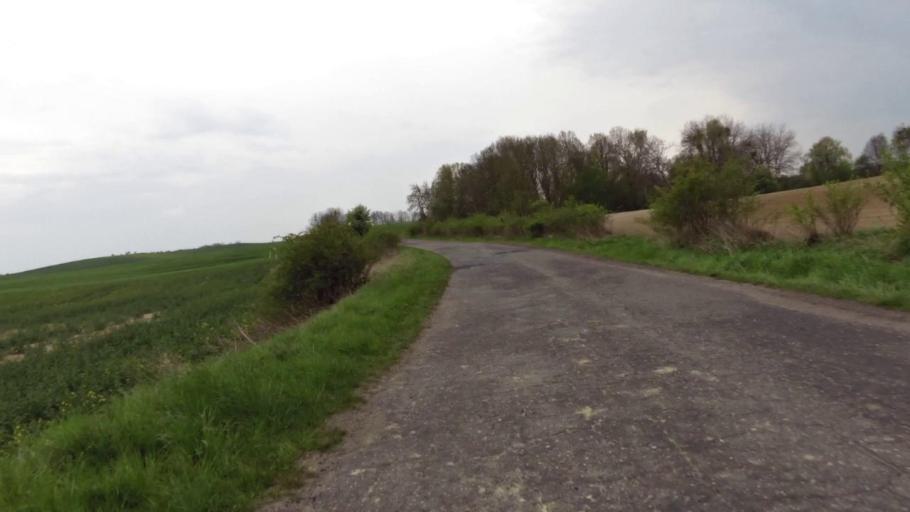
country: PL
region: West Pomeranian Voivodeship
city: Trzcinsko Zdroj
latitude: 52.9516
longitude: 14.6933
